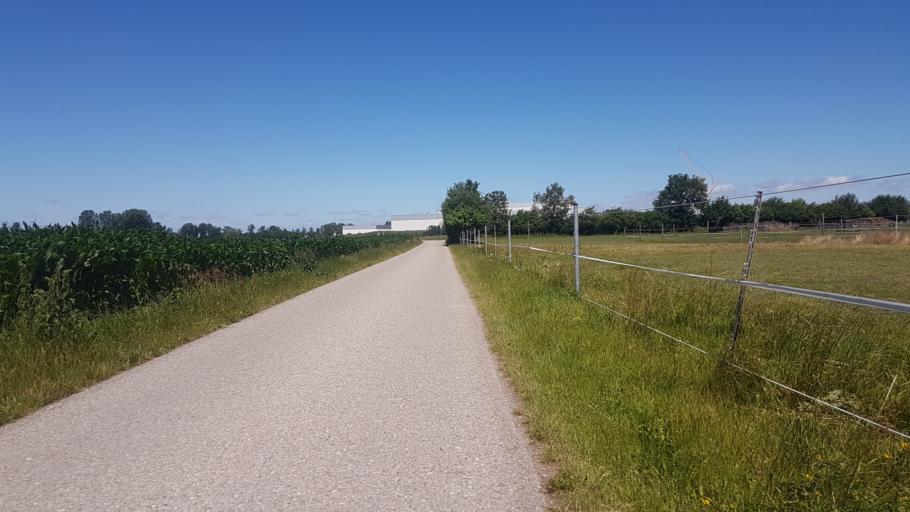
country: DE
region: Bavaria
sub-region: Regierungsbezirk Mittelfranken
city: Herrieden
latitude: 49.2244
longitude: 10.5131
